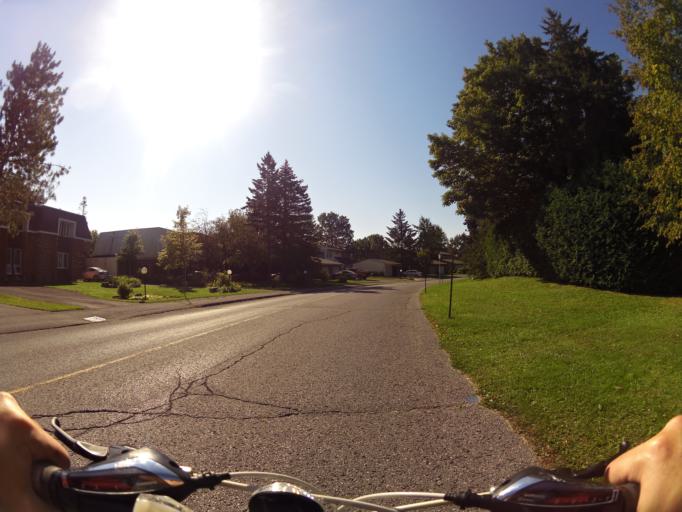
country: CA
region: Ontario
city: Bells Corners
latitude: 45.3267
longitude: -75.8908
